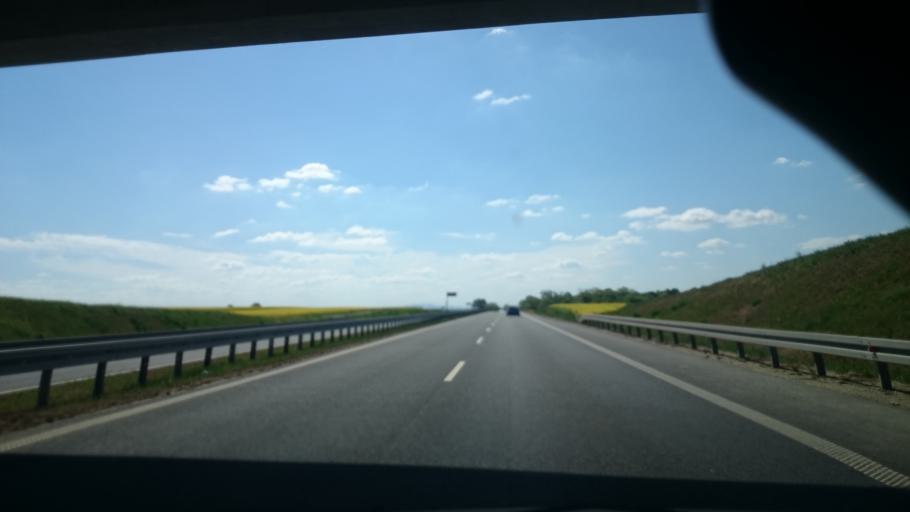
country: PL
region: Opole Voivodeship
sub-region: Powiat nyski
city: Nysa
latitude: 50.5003
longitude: 17.3002
